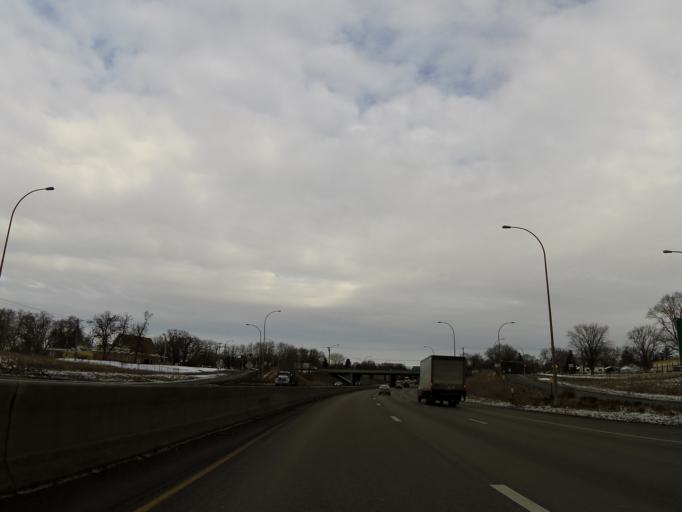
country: US
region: Minnesota
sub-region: Hennepin County
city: Bloomington
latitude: 44.8387
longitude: -93.2980
